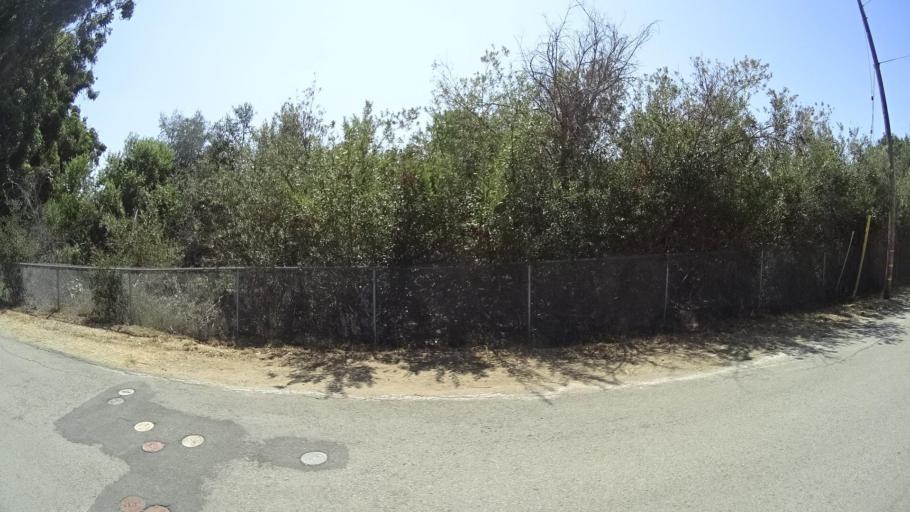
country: US
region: California
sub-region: San Diego County
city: Lake San Marcos
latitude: 33.1577
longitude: -117.2124
